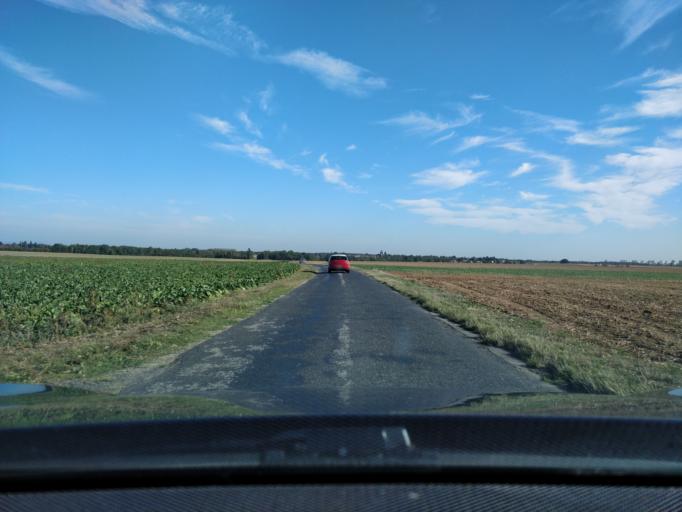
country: FR
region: Ile-de-France
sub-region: Departement de l'Essonne
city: Gometz-la-Ville
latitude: 48.6567
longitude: 2.1135
